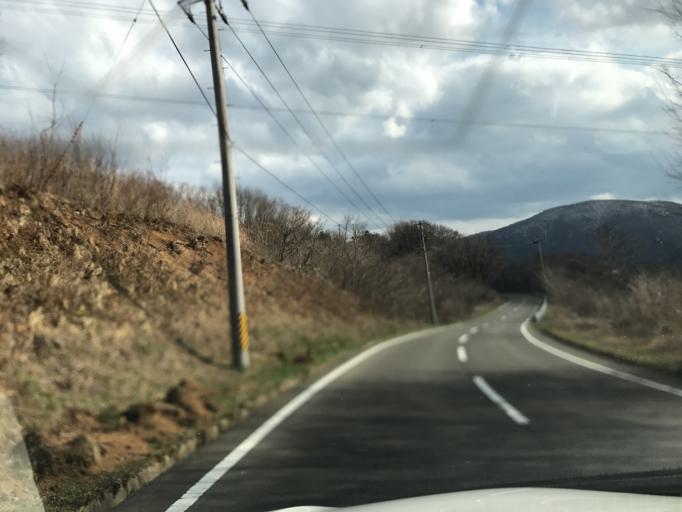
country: JP
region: Miyagi
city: Shiroishi
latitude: 38.0354
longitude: 140.5368
